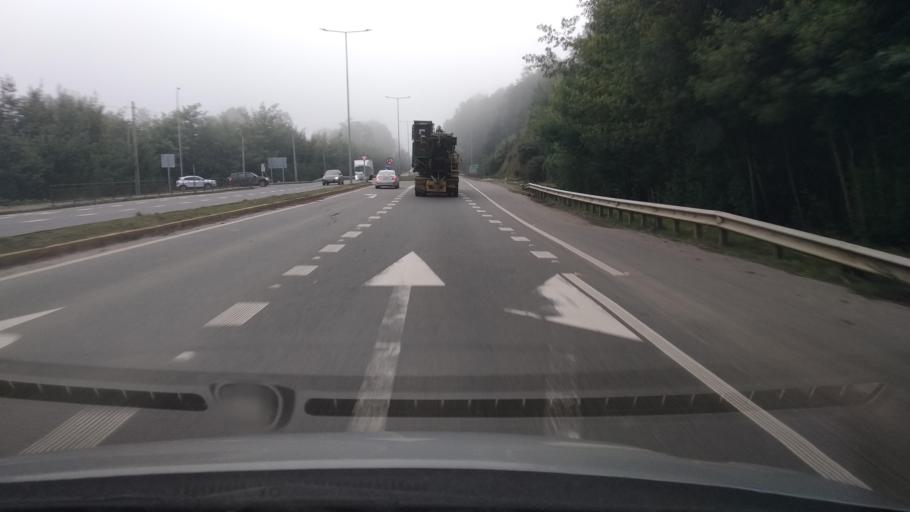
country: CL
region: Los Lagos
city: Las Animas
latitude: -39.7627
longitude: -73.2282
